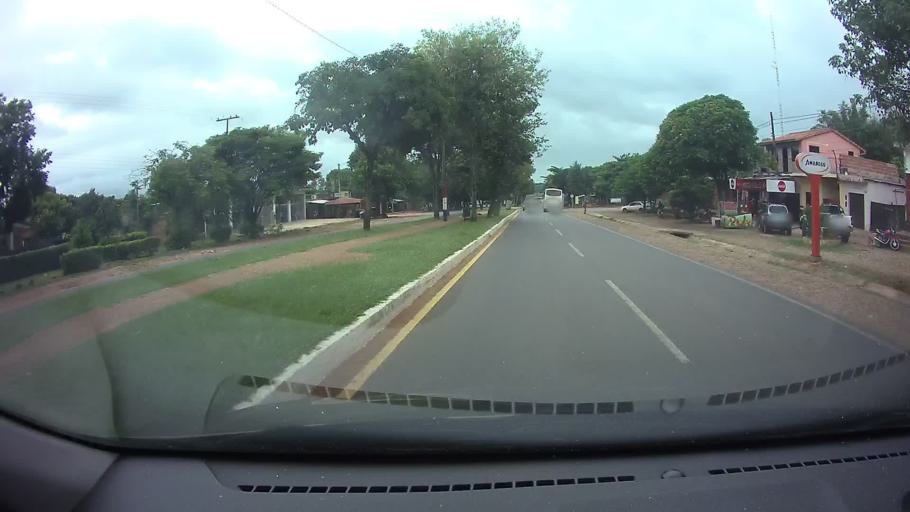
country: PY
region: Central
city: Nueva Italia
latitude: -25.6121
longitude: -57.4657
